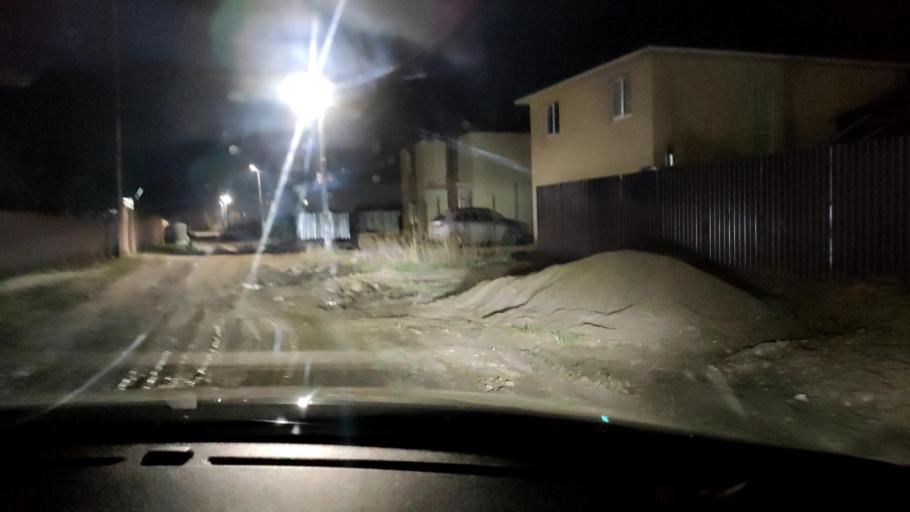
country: RU
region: Tatarstan
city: Stolbishchi
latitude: 55.6804
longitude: 49.2083
